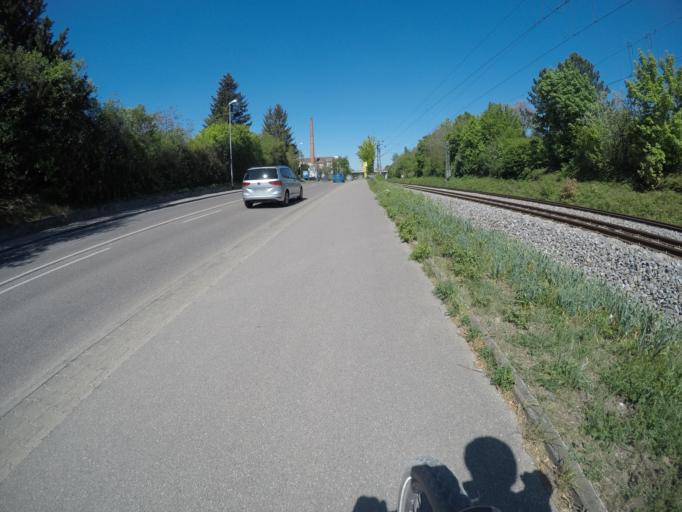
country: DE
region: Baden-Wuerttemberg
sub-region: Regierungsbezirk Stuttgart
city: Waiblingen
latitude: 48.8195
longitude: 9.3136
